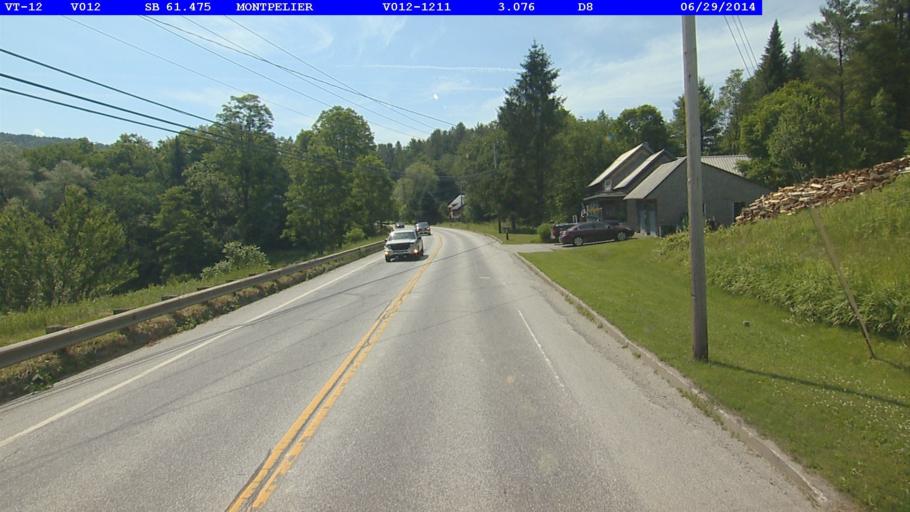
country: US
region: Vermont
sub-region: Washington County
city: Montpelier
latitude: 44.2864
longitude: -72.5778
